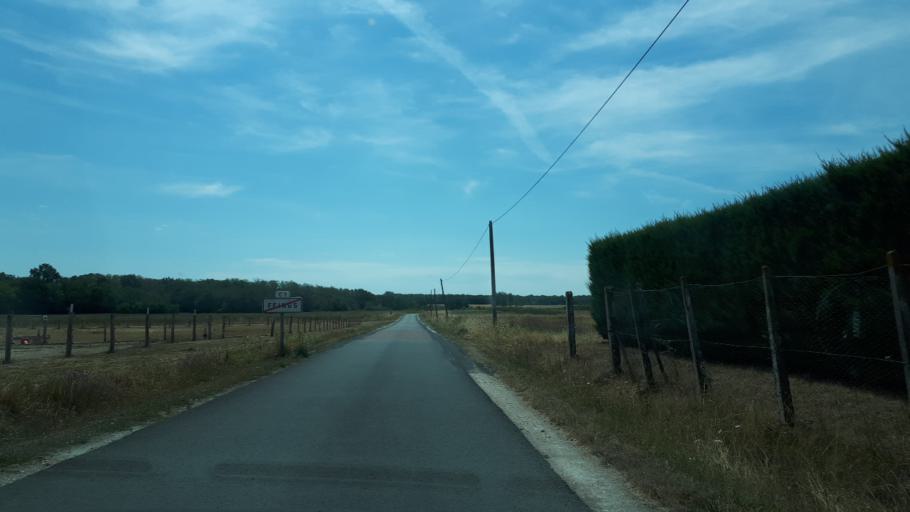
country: FR
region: Centre
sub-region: Departement du Loir-et-Cher
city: Chitenay
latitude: 47.4356
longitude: 1.3546
